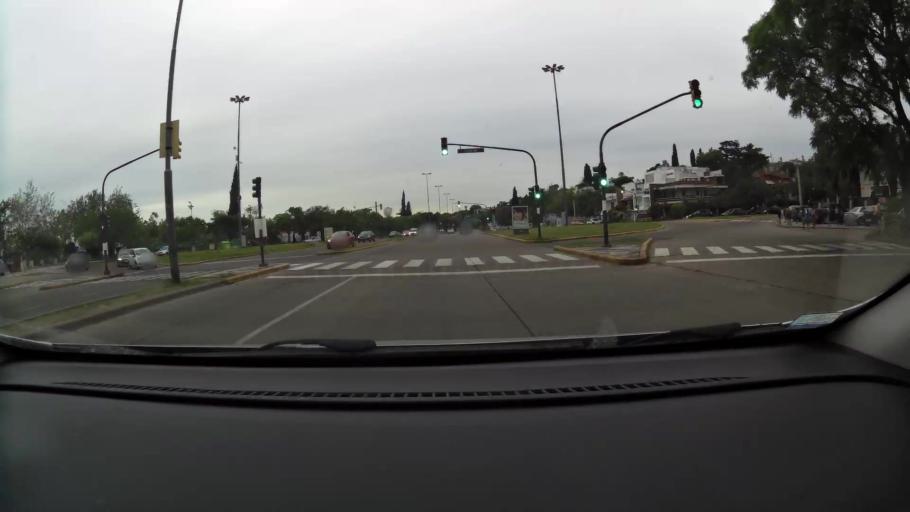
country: AR
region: Santa Fe
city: Granadero Baigorria
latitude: -32.8930
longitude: -60.6856
